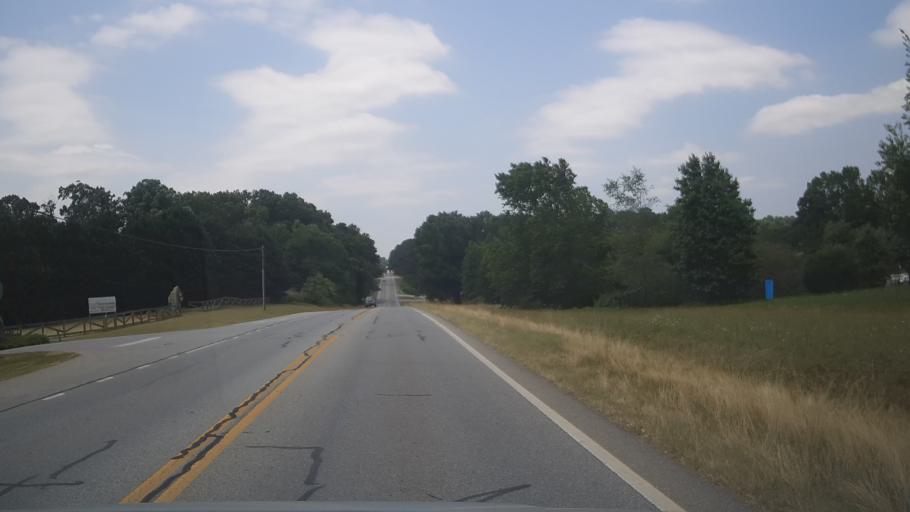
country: US
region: Georgia
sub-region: Jackson County
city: Commerce
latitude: 34.1854
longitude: -83.3944
